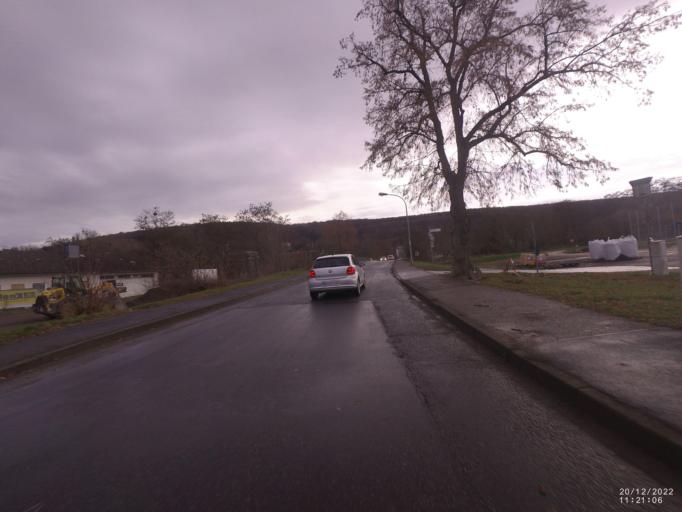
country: DE
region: Rheinland-Pfalz
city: Remagen
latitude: 50.5517
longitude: 7.2173
